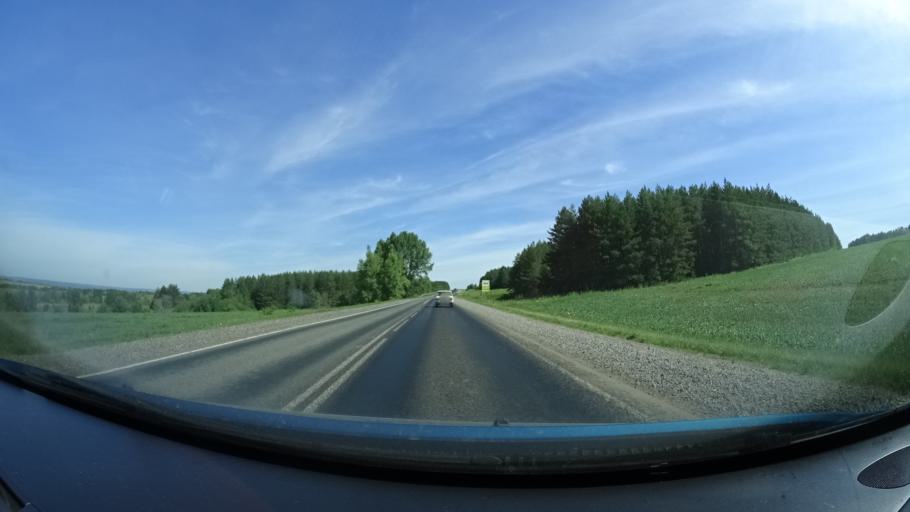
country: RU
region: Bashkortostan
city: Blagoveshchensk
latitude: 55.1343
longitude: 55.8442
